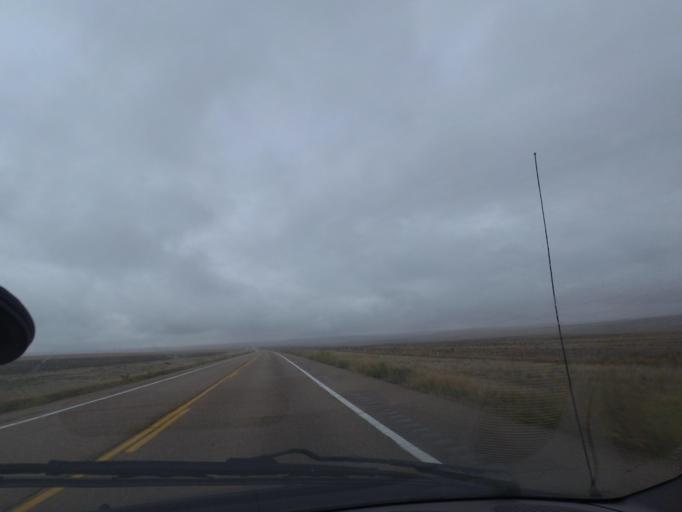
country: US
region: Colorado
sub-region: Arapahoe County
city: Byers
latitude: 39.7330
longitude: -103.8821
